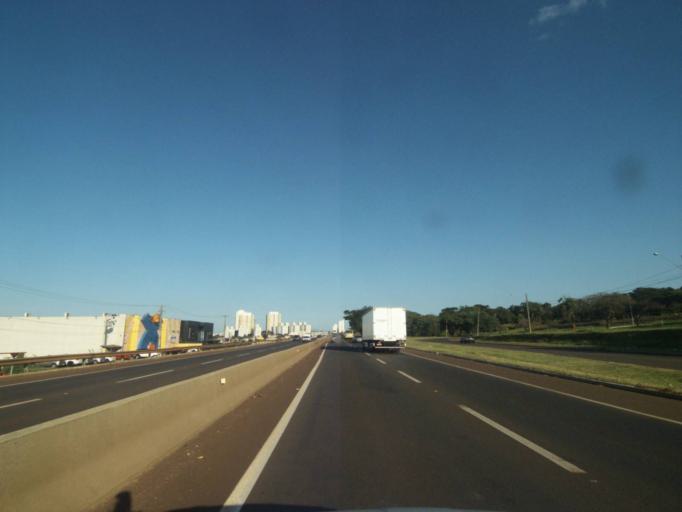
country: BR
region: Parana
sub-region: Londrina
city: Londrina
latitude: -23.3217
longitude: -51.2023
